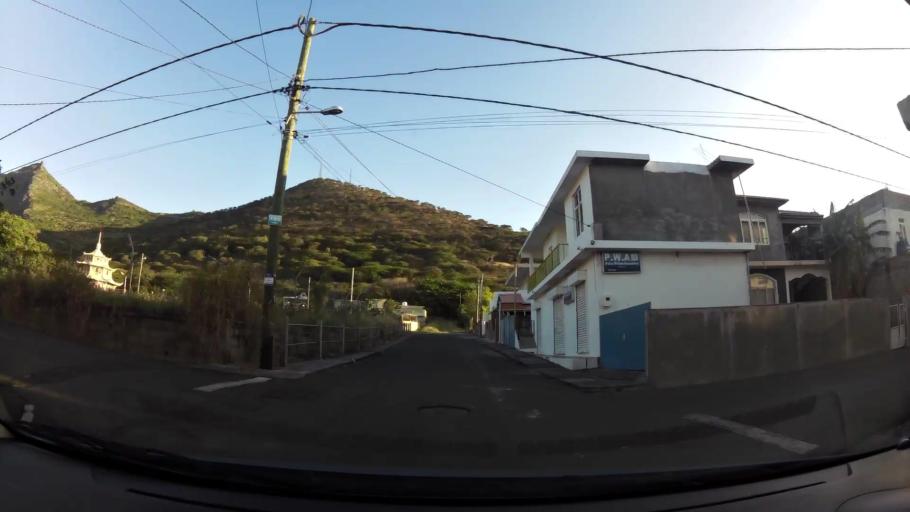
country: MU
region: Port Louis
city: Port Louis
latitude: -20.1752
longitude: 57.5070
